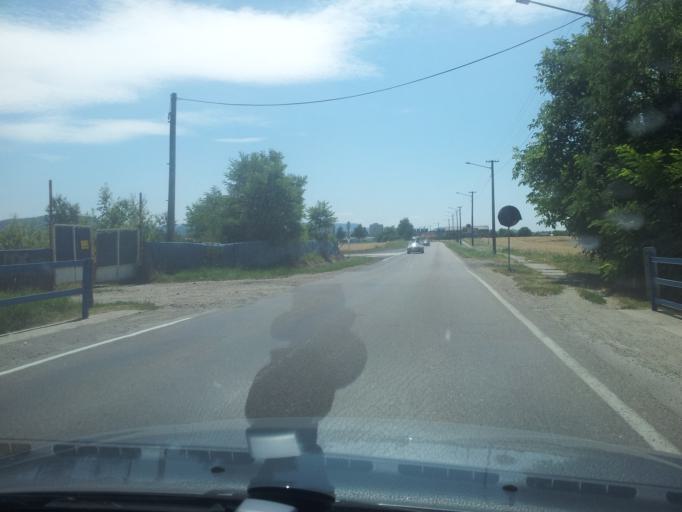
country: SK
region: Nitriansky
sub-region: Okres Nove Zamky
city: Sturovo
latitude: 47.8097
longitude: 18.7046
